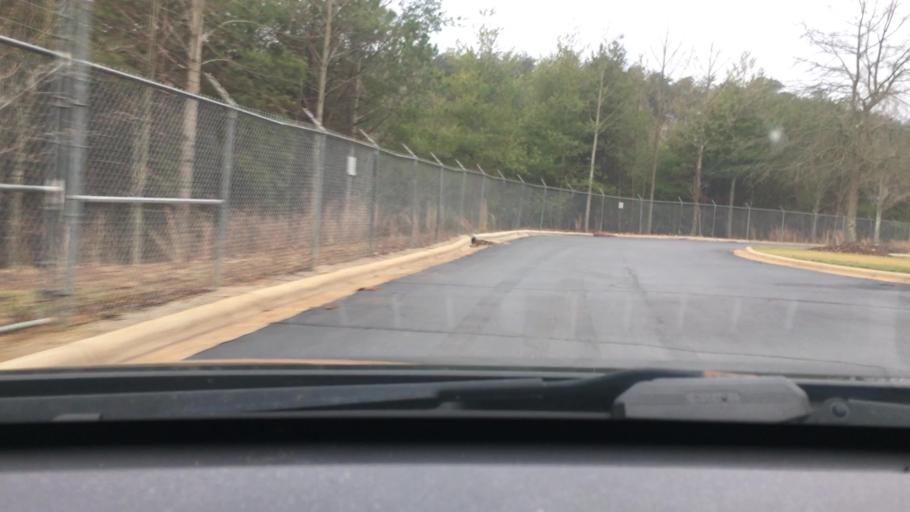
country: US
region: North Carolina
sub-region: McDowell County
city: West Marion
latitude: 35.6408
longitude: -81.9907
